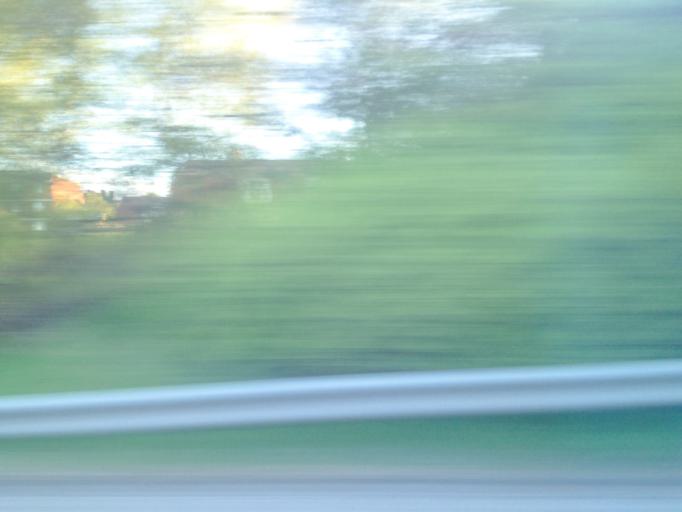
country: FI
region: Haeme
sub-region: Haemeenlinna
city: Haemeenlinna
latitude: 60.9967
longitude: 24.4538
